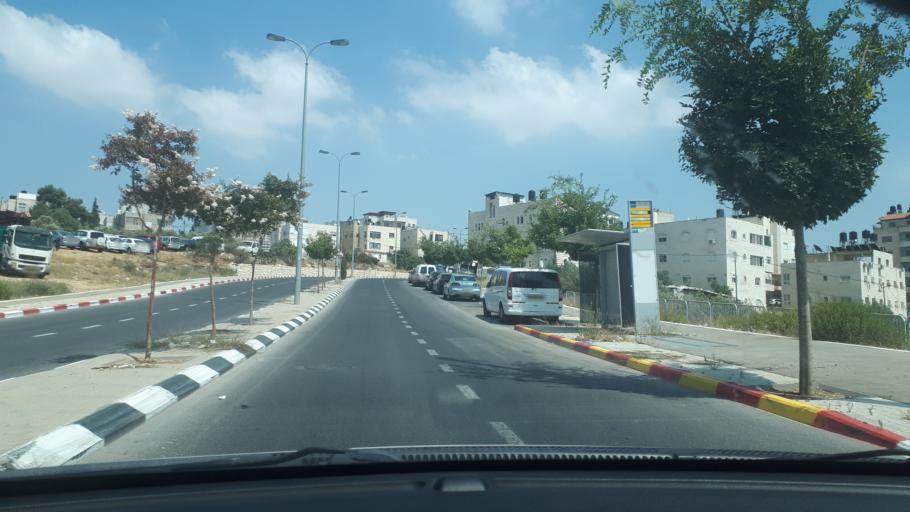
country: PS
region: West Bank
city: Ar Ram wa Dahiyat al Barid
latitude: 31.8181
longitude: 35.2250
